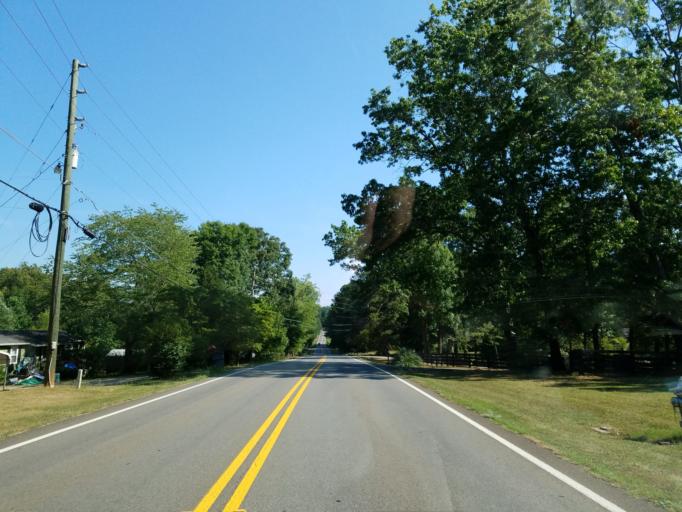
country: US
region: Georgia
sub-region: Fulton County
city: Milton
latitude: 34.2130
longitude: -84.2895
